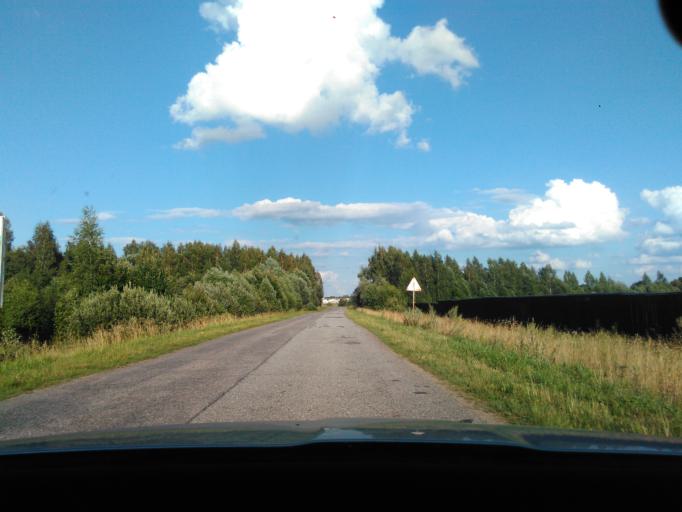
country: RU
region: Tverskaya
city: Zavidovo
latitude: 56.6094
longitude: 36.5574
